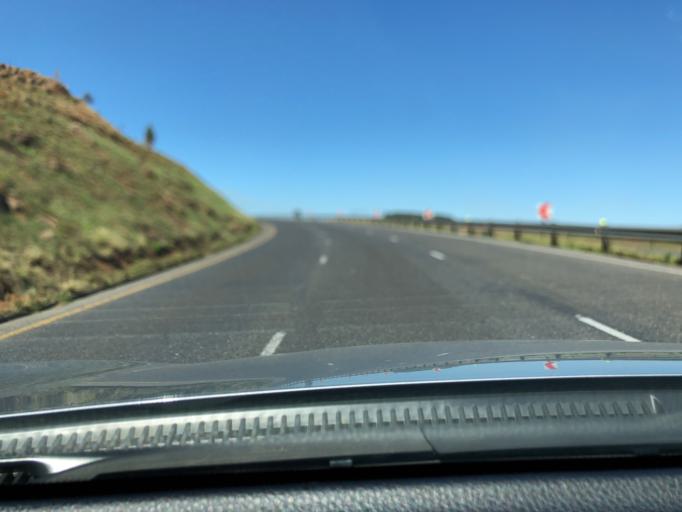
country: ZA
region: KwaZulu-Natal
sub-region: uMgungundlovu District Municipality
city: Howick
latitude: -29.4357
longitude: 30.1717
